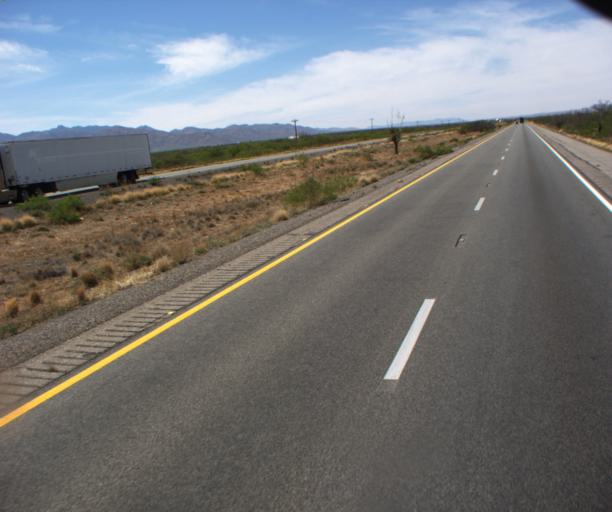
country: US
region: Arizona
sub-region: Cochise County
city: Willcox
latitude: 32.3092
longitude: -109.4052
